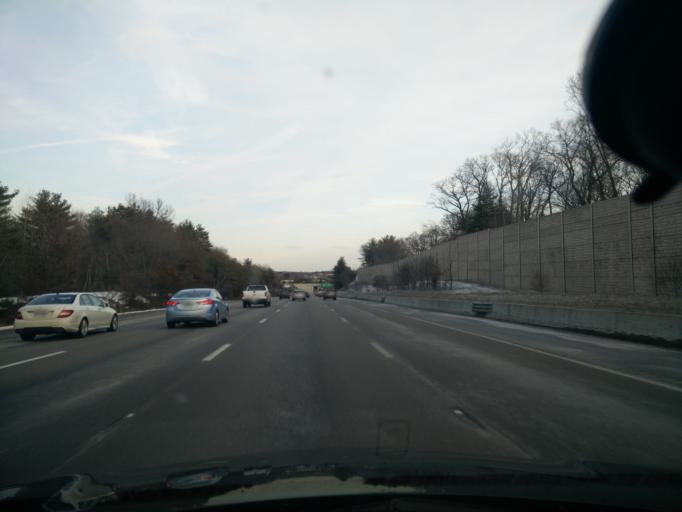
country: US
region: Massachusetts
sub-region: Norfolk County
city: Dedham
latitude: 42.2329
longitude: -71.1900
